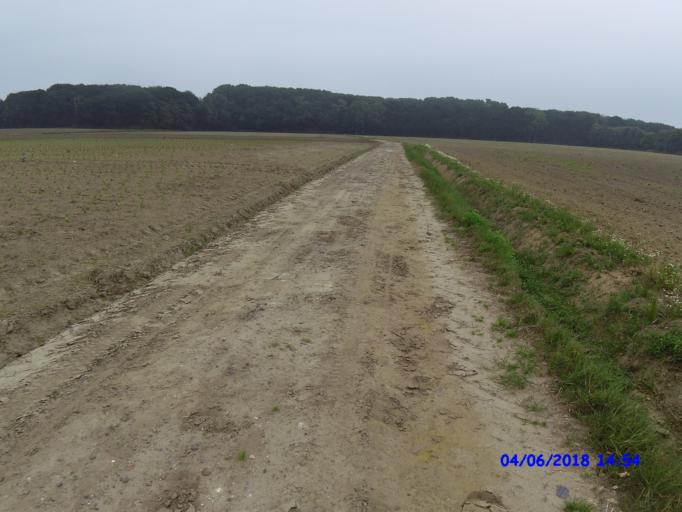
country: BE
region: Flanders
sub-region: Provincie West-Vlaanderen
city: Ardooie
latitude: 50.9571
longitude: 3.2234
